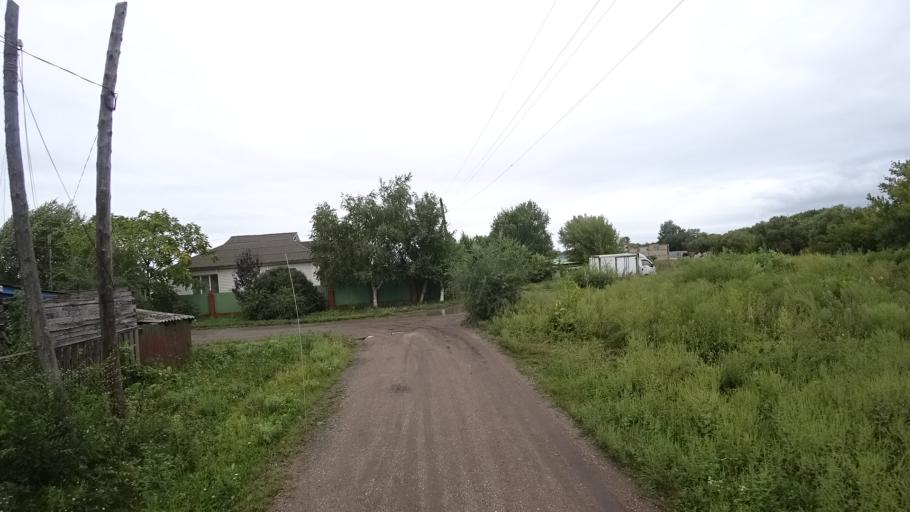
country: RU
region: Primorskiy
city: Chernigovka
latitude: 44.3492
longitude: 132.5779
